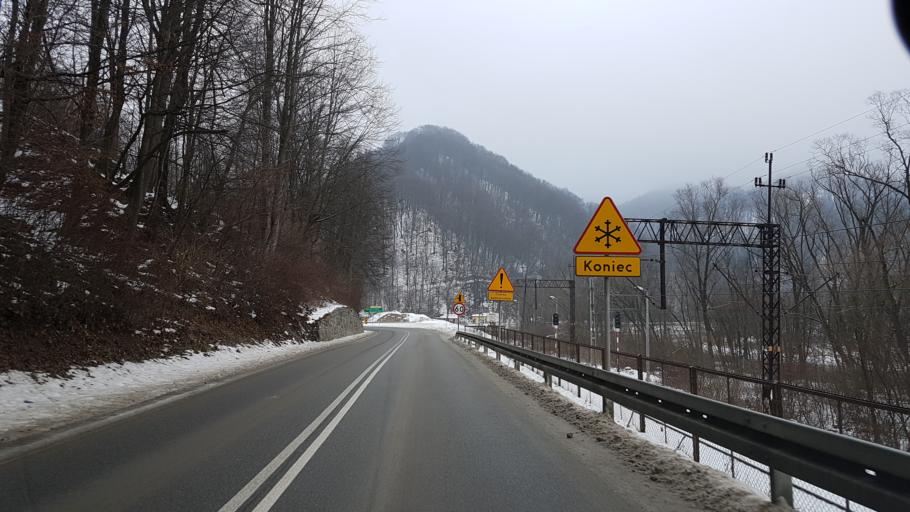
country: PL
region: Lesser Poland Voivodeship
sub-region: Powiat nowosadecki
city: Piwniczna-Zdroj
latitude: 49.4031
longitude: 20.7511
